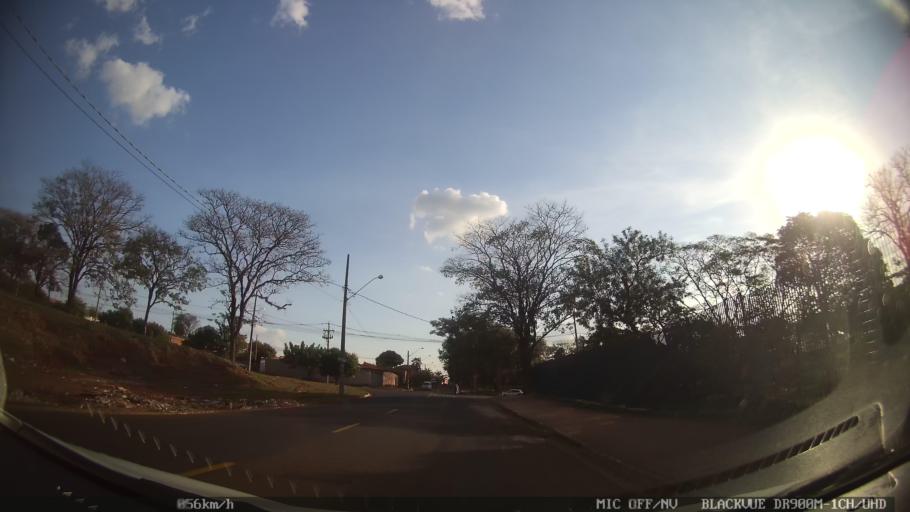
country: BR
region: Sao Paulo
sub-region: Ribeirao Preto
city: Ribeirao Preto
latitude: -21.1527
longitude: -47.8414
